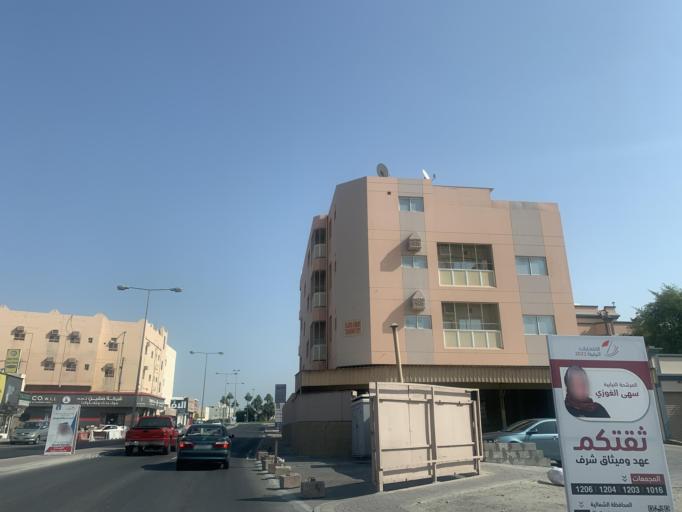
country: BH
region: Central Governorate
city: Madinat Hamad
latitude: 26.1404
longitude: 50.4969
